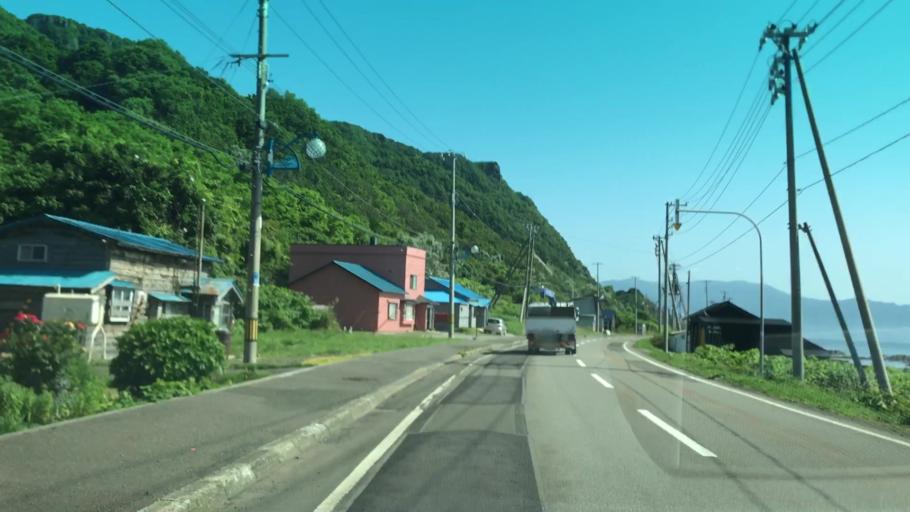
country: JP
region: Hokkaido
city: Iwanai
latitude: 43.0947
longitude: 140.4634
